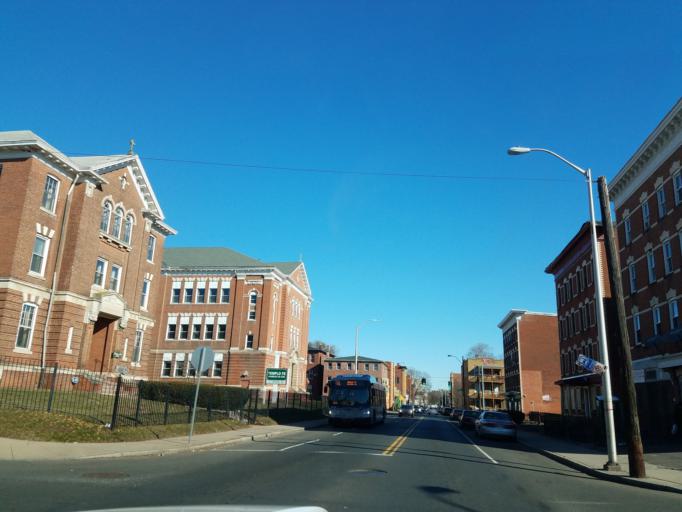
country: US
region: Connecticut
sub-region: Hartford County
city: Hartford
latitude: 41.7553
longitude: -72.6871
